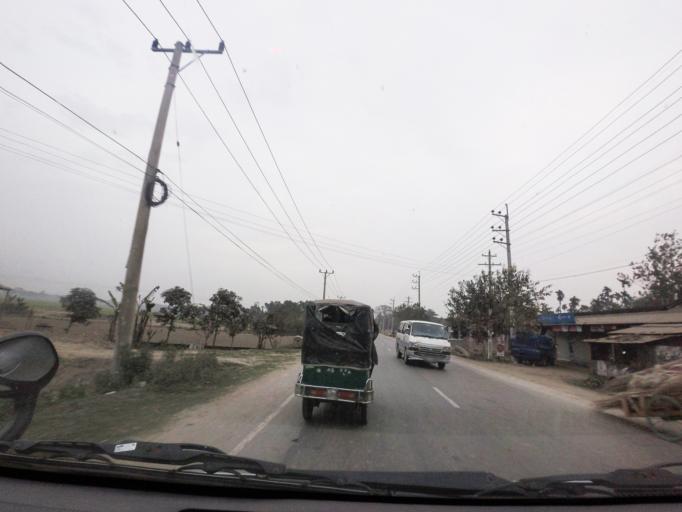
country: BD
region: Dhaka
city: Bajitpur
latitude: 24.2468
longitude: 90.8059
